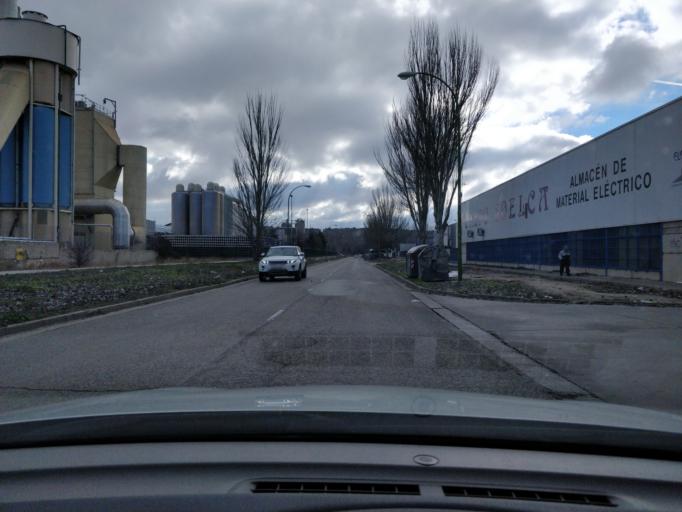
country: ES
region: Castille and Leon
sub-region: Provincia de Burgos
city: Burgos
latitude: 42.3495
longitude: -3.6582
